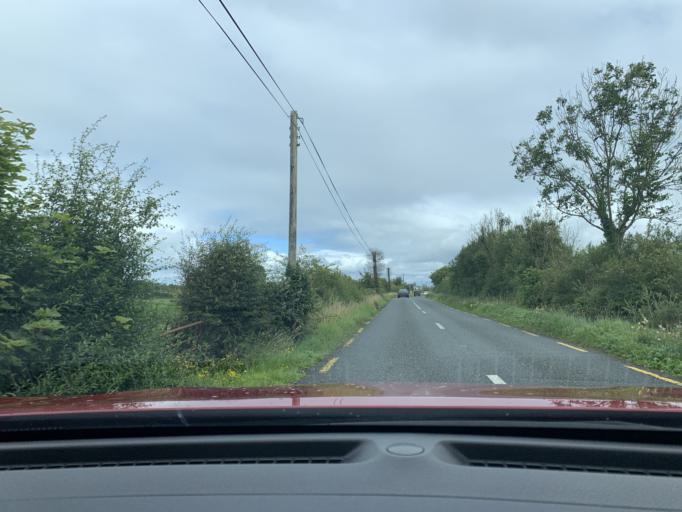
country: IE
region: Connaught
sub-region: County Leitrim
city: Carrick-on-Shannon
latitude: 53.8940
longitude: -8.1463
